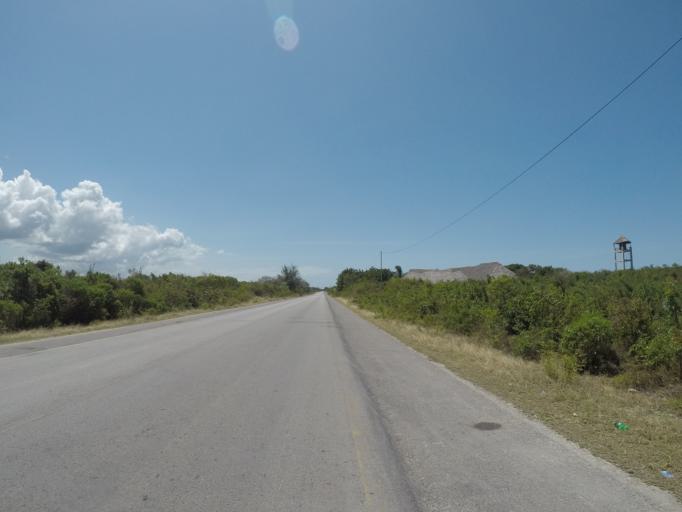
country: TZ
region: Zanzibar Central/South
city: Nganane
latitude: -6.2982
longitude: 39.5381
